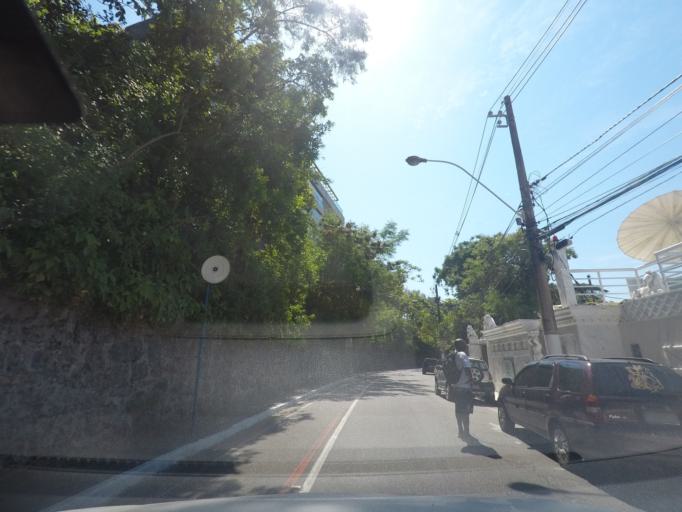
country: BR
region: Rio de Janeiro
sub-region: Niteroi
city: Niteroi
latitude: -22.9149
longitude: -43.1092
